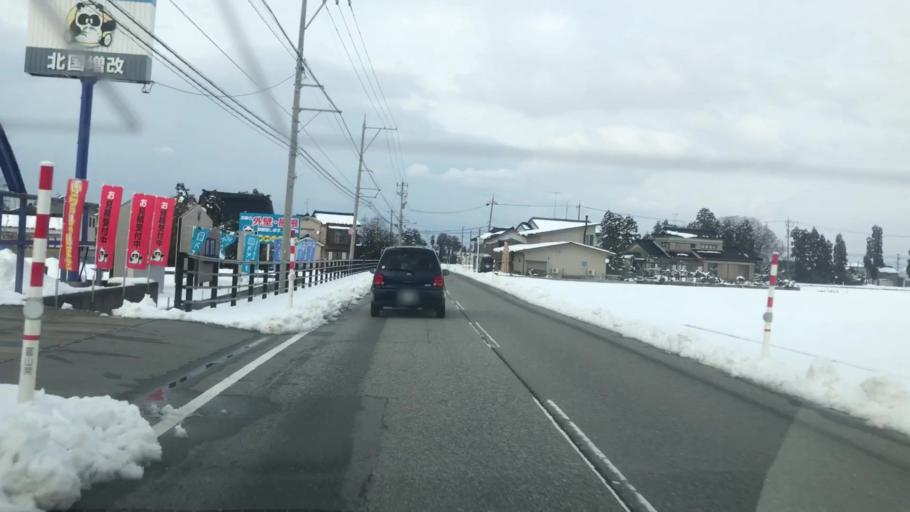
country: JP
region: Toyama
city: Toyama-shi
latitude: 36.6733
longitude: 137.2893
